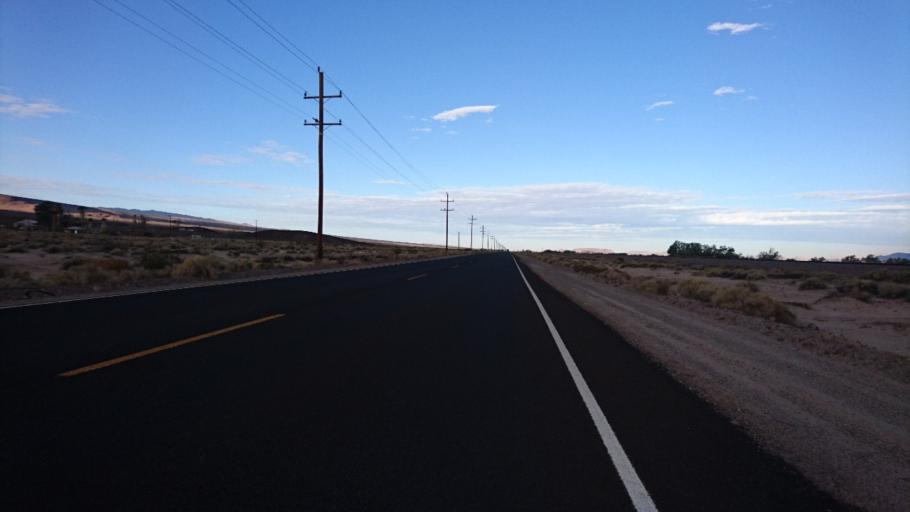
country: US
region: California
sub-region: San Bernardino County
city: Barstow
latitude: 34.8373
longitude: -116.7212
